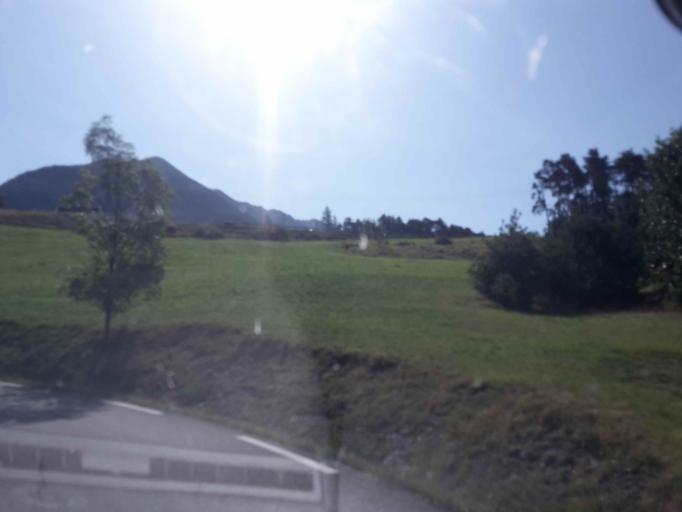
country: FR
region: Provence-Alpes-Cote d'Azur
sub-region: Departement des Hautes-Alpes
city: Guillestre
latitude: 44.6362
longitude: 6.6684
